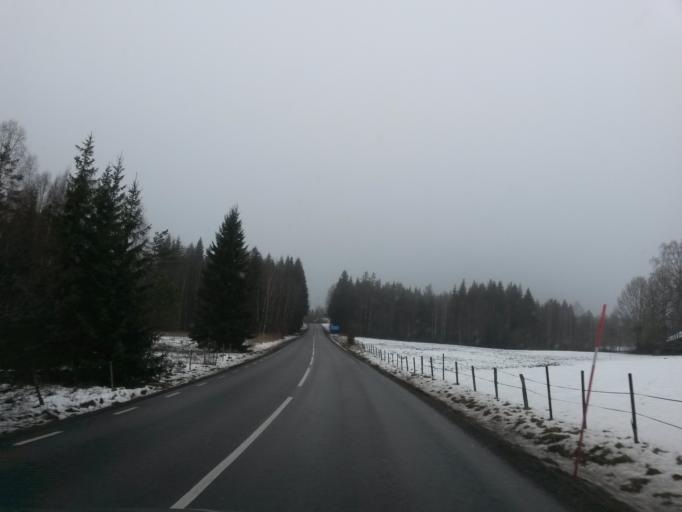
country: SE
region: Vaestra Goetaland
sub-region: Ulricehamns Kommun
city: Ulricehamn
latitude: 57.6710
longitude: 13.4022
